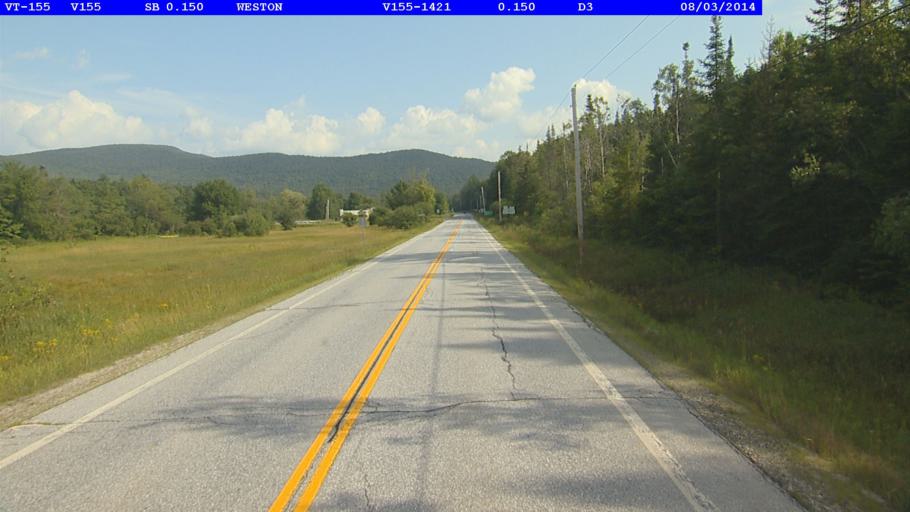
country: US
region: Vermont
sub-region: Windsor County
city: Chester
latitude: 43.3388
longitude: -72.7869
